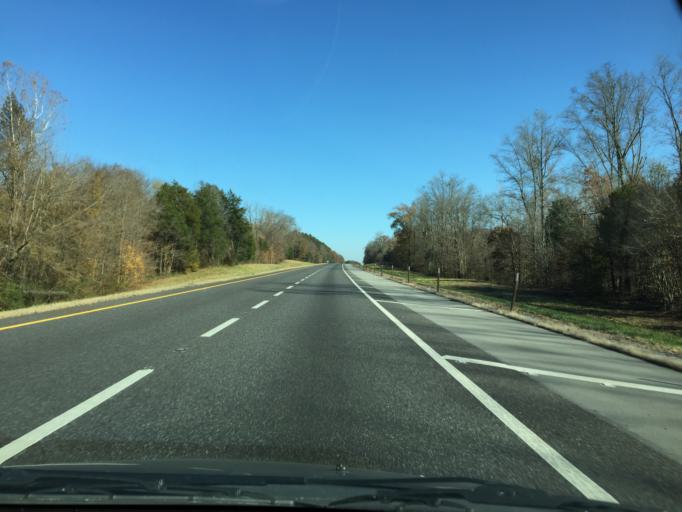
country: US
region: Tennessee
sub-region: Meigs County
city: Decatur
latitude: 35.3462
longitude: -84.7492
